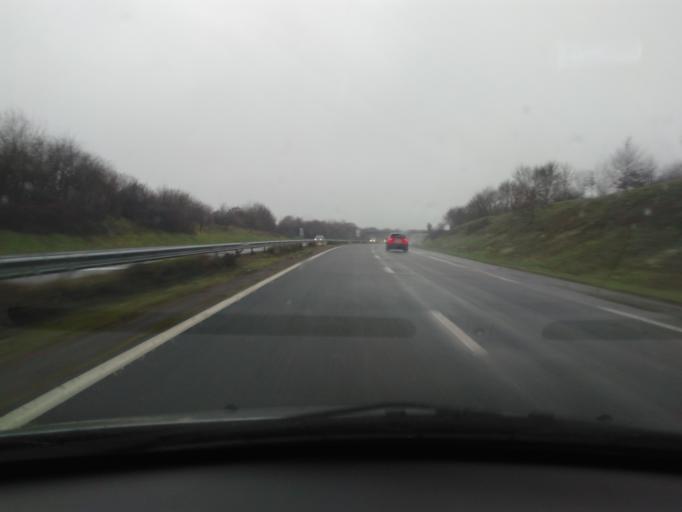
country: FR
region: Pays de la Loire
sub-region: Departement de la Vendee
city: Bournezeau
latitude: 46.6299
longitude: -1.1730
